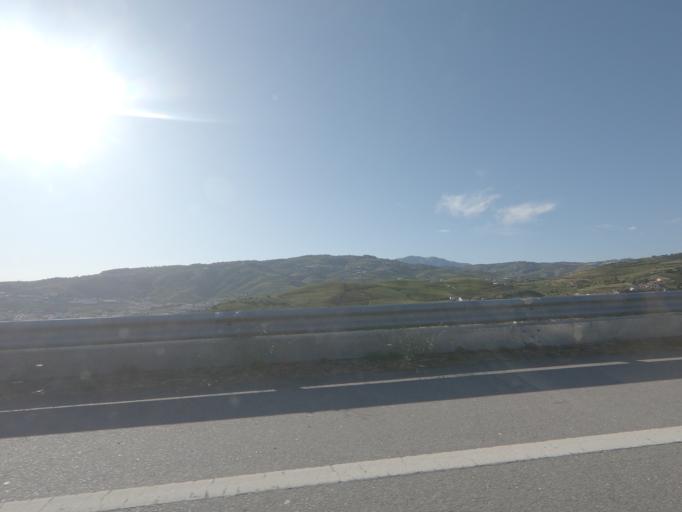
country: PT
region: Vila Real
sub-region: Santa Marta de Penaguiao
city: Santa Marta de Penaguiao
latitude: 41.1951
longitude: -7.7989
